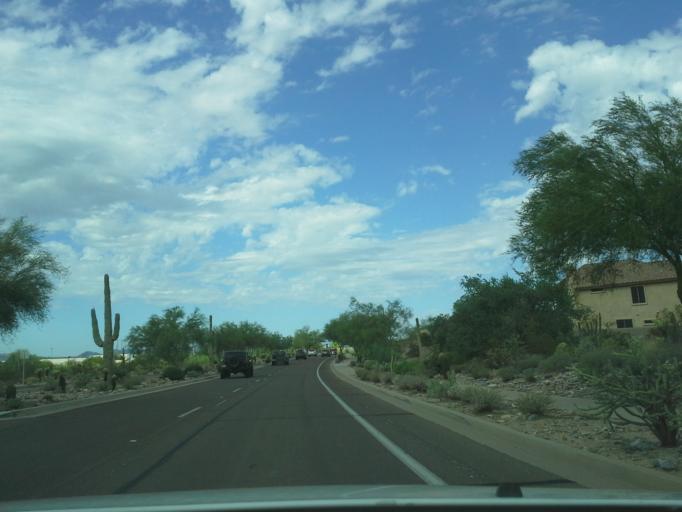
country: US
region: Arizona
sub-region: Maricopa County
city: Scottsdale
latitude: 33.6282
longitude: -111.8570
